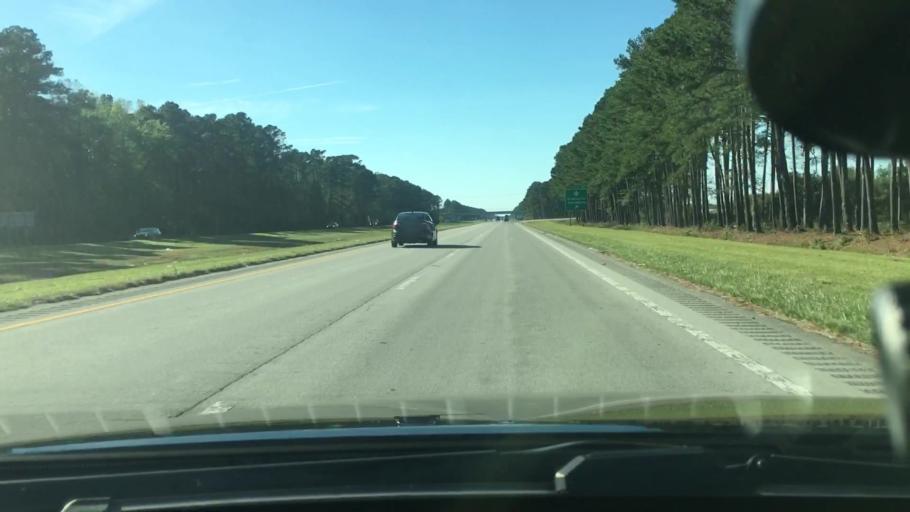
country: US
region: North Carolina
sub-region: Craven County
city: Trent Woods
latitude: 35.1243
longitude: -77.1244
